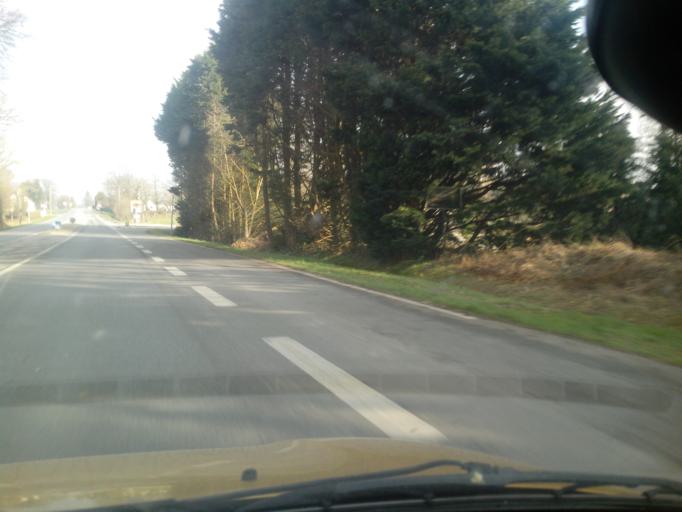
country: FR
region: Brittany
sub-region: Departement du Morbihan
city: Questembert
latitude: 47.6874
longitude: -2.4617
